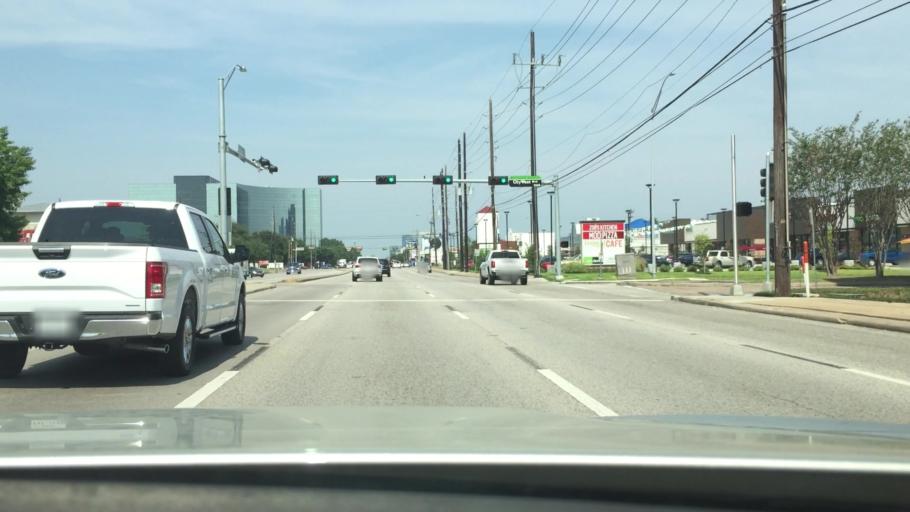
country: US
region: Texas
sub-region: Harris County
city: Bunker Hill Village
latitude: 29.7370
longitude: -95.5605
